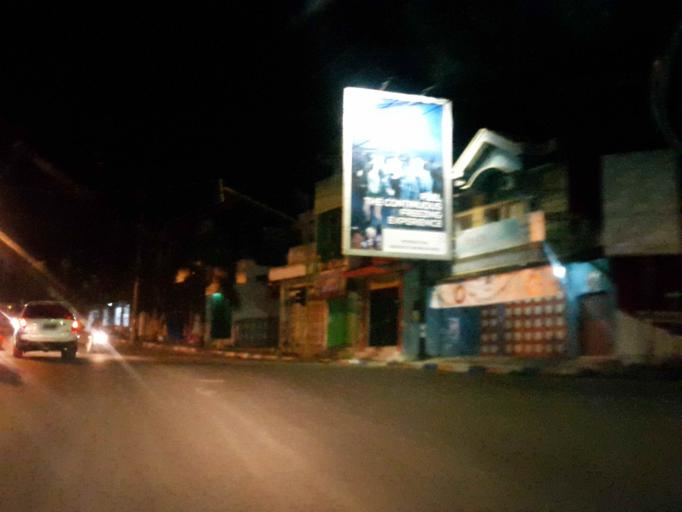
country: ID
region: Central Java
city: Sawahan
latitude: -6.7091
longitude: 111.3413
